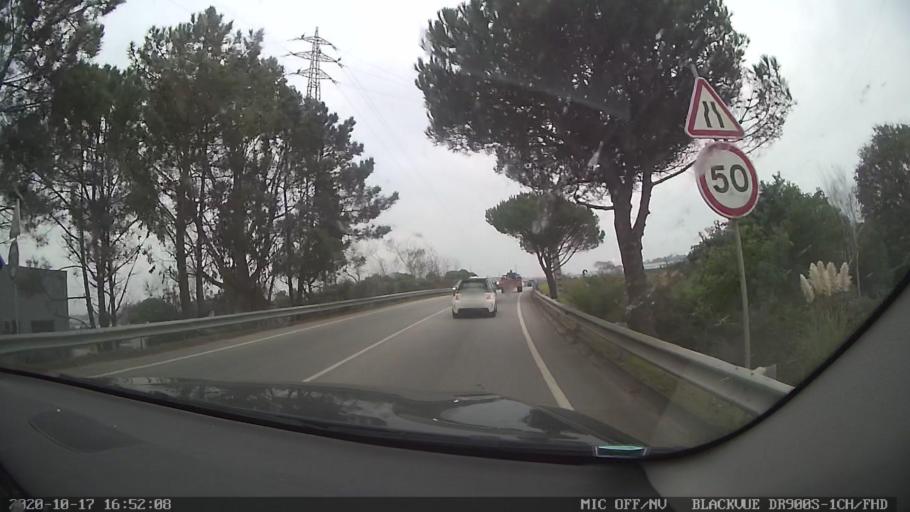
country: PT
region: Braga
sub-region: Esposende
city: Esposende
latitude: 41.5176
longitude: -8.7705
